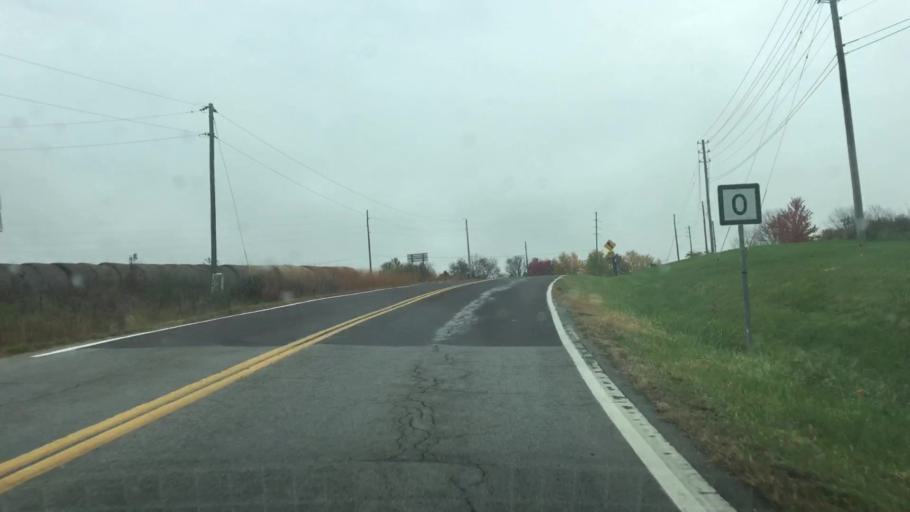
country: US
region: Missouri
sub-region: Callaway County
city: Fulton
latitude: 38.8403
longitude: -91.9235
